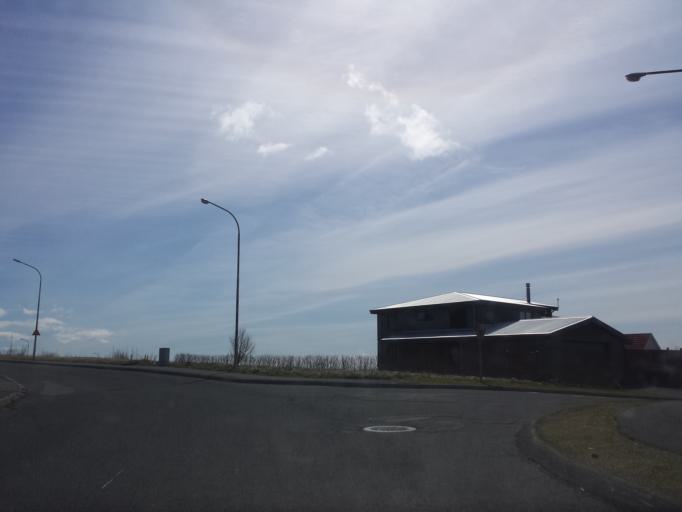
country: IS
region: South
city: Hveragerdi
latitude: 64.0062
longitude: -21.1877
